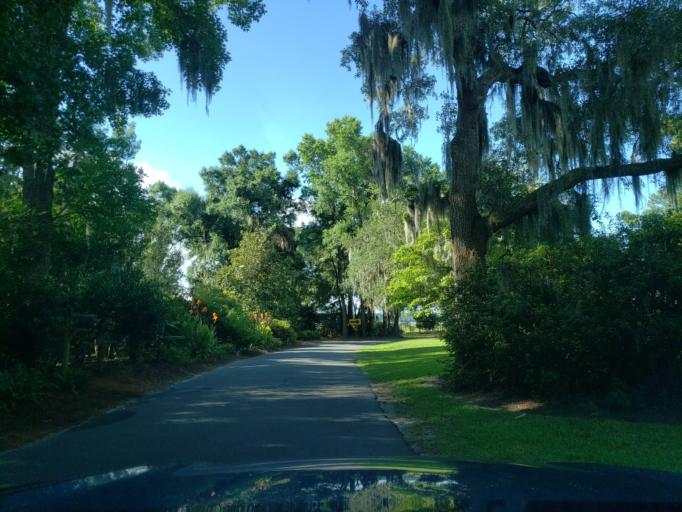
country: US
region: Georgia
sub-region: Chatham County
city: Isle of Hope
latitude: 31.9742
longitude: -81.0577
